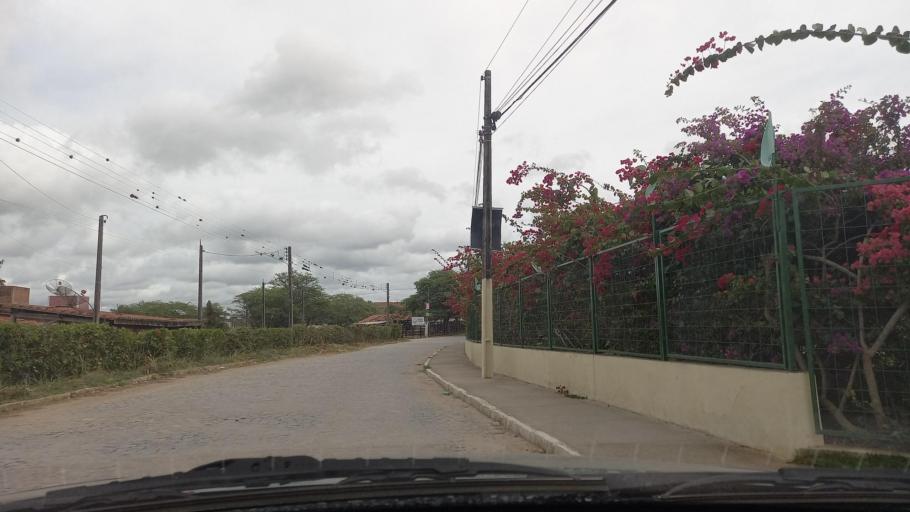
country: ET
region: Oromiya
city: Gore
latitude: 8.1937
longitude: 35.5762
